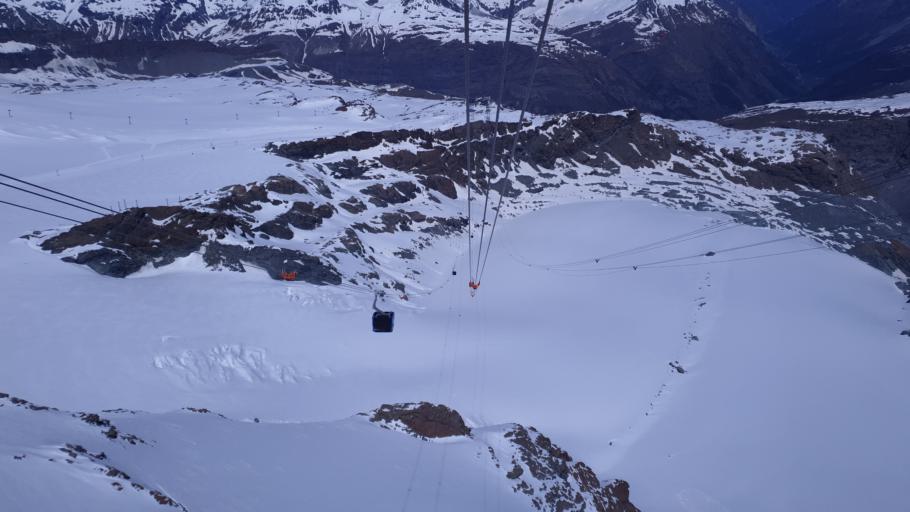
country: CH
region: Valais
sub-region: Visp District
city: Zermatt
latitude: 45.9432
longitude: 7.7282
